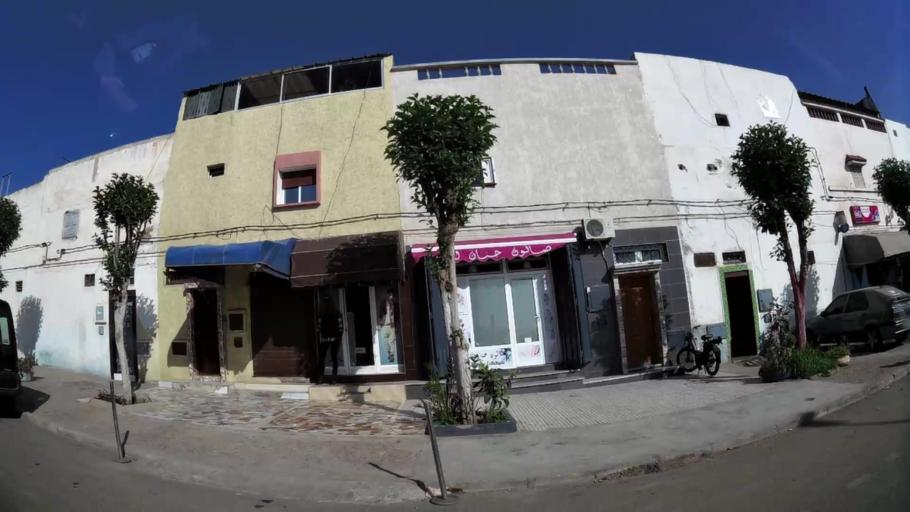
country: MA
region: Oued ed Dahab-Lagouira
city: Dakhla
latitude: 30.4213
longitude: -9.5734
